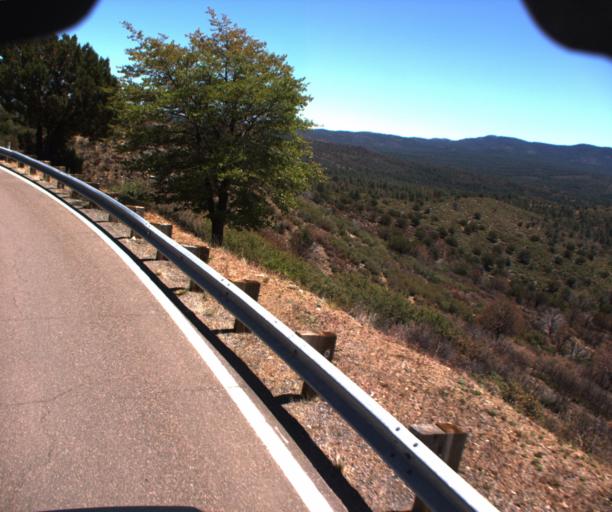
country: US
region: Arizona
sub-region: Yavapai County
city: Prescott
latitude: 34.4735
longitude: -112.5110
